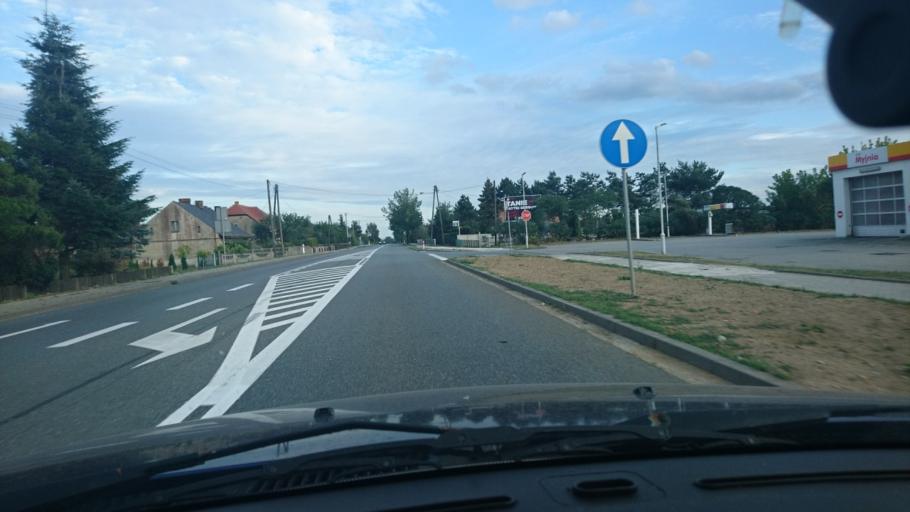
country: PL
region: Opole Voivodeship
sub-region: Powiat oleski
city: Olesno
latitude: 50.8833
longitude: 18.4070
